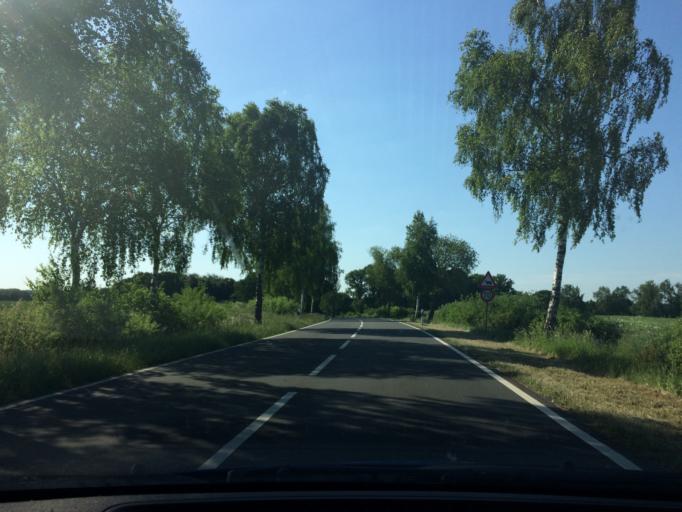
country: DE
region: Lower Saxony
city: Bomlitz
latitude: 52.9220
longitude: 9.6980
